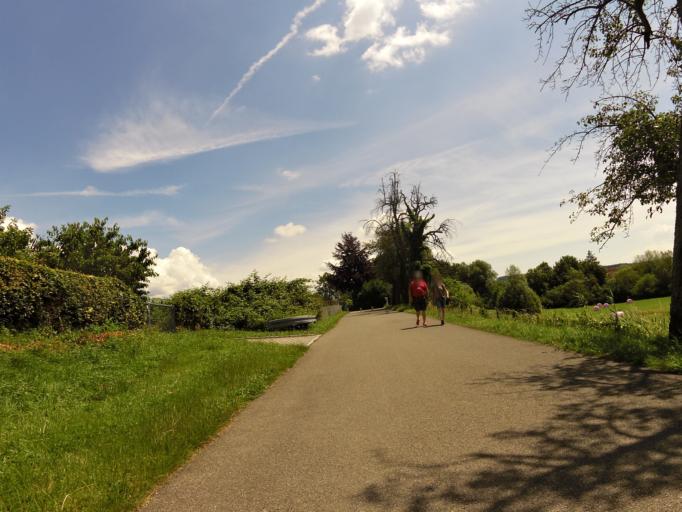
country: DE
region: Baden-Wuerttemberg
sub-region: Tuebingen Region
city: Uhldingen-Muhlhofen
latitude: 47.7436
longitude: 9.2207
